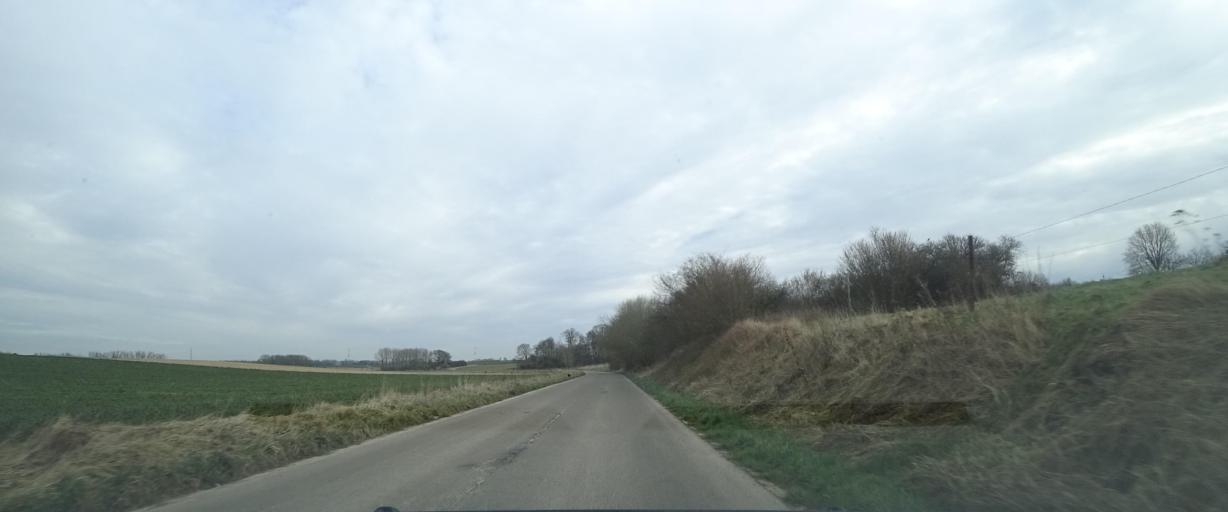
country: BE
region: Wallonia
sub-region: Province de Namur
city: Sombreffe
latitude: 50.4812
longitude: 4.6301
